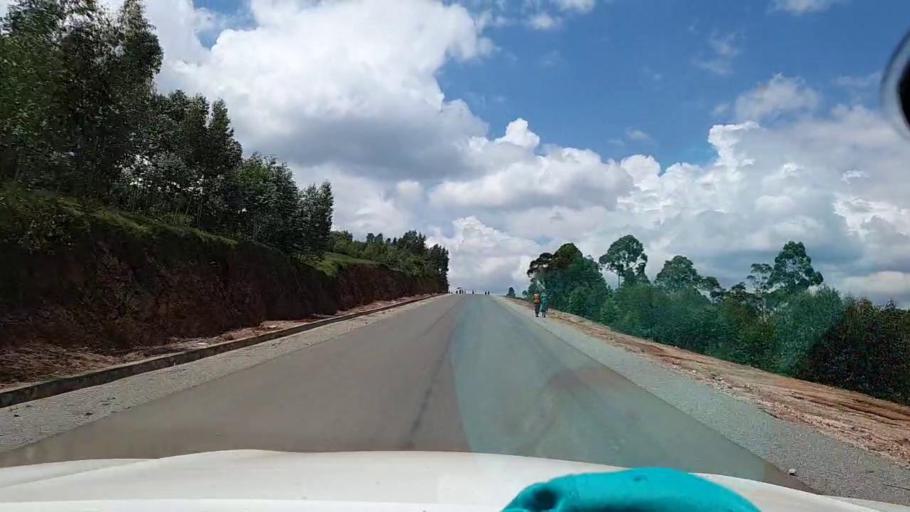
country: RW
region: Southern Province
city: Nzega
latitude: -2.6432
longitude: 29.5743
